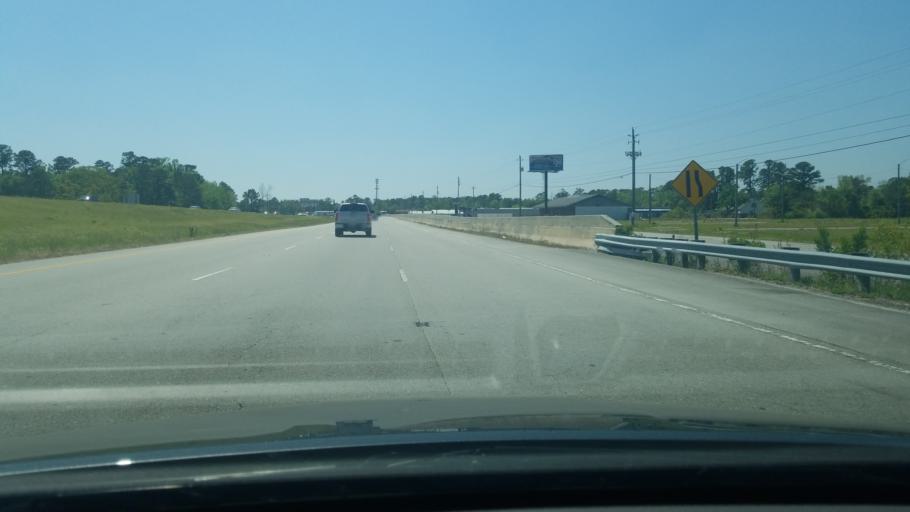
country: US
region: North Carolina
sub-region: Onslow County
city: Jacksonville
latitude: 34.7396
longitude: -77.4622
